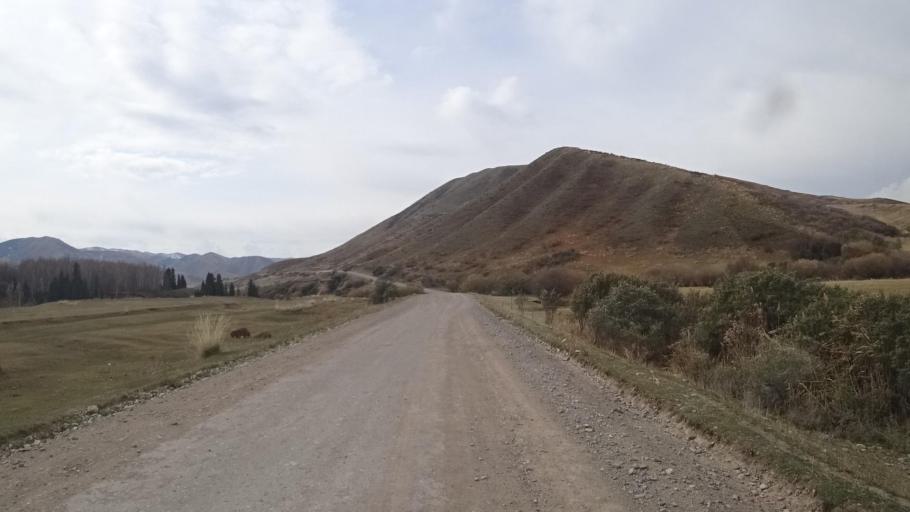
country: KG
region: Ysyk-Koel
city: Teploklyuchenka
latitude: 42.7355
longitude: 78.8319
